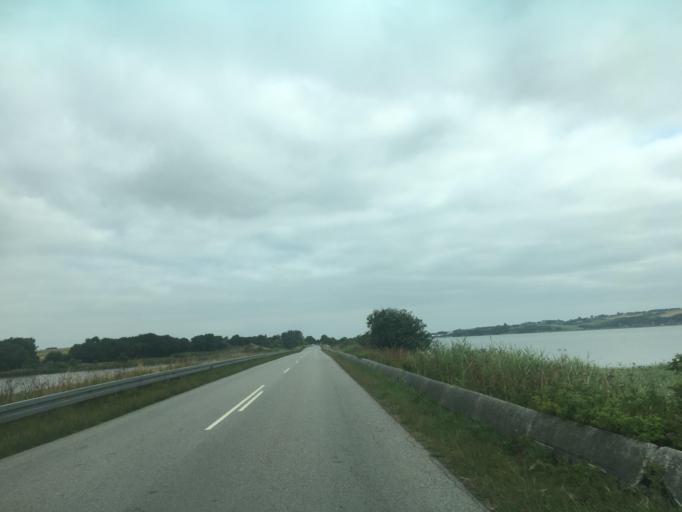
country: DK
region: North Denmark
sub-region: Thisted Kommune
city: Thisted
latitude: 56.8703
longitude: 8.6224
